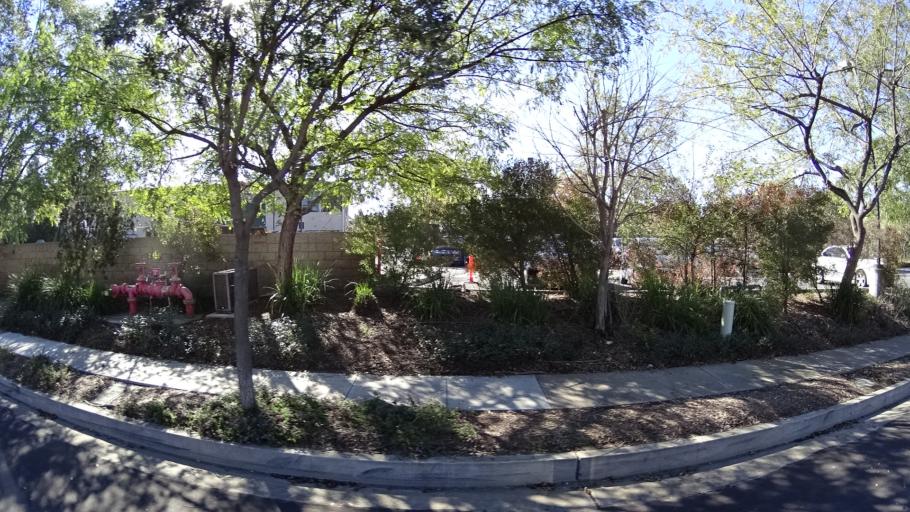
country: US
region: California
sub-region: Orange County
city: Villa Park
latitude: 33.8389
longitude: -117.8275
